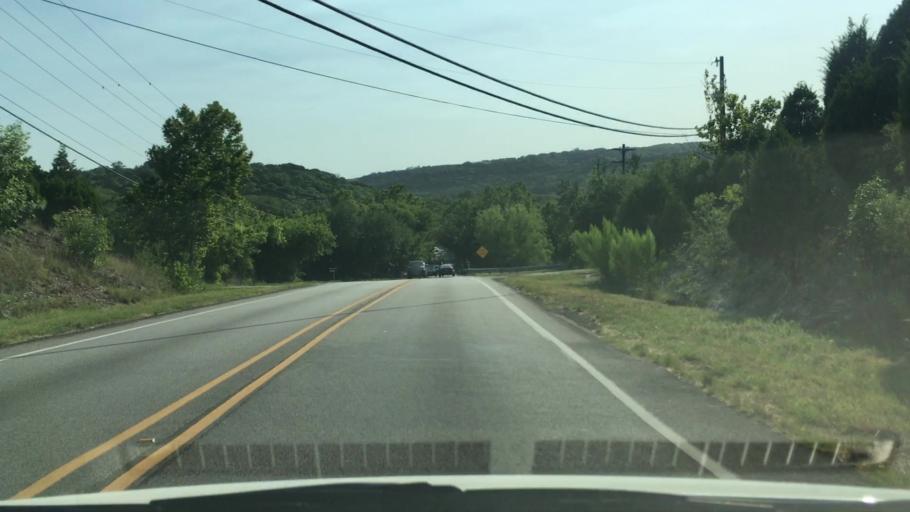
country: US
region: Texas
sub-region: Williamson County
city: Anderson Mill
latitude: 30.4524
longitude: -97.8492
